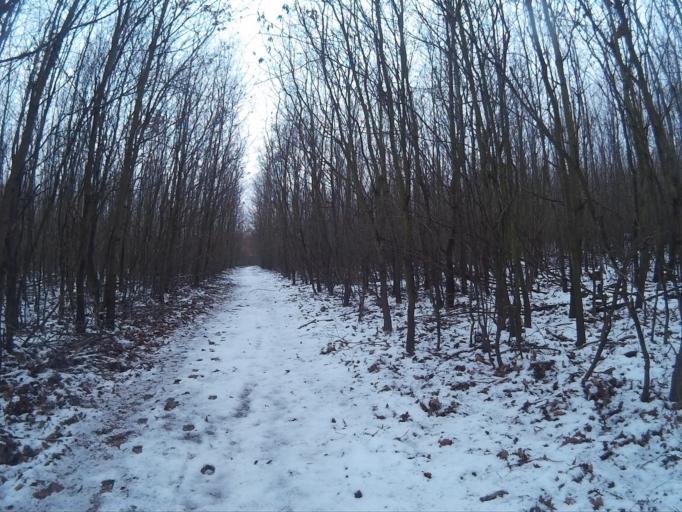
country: HU
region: Komarom-Esztergom
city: Tarjan
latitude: 47.5880
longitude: 18.5140
